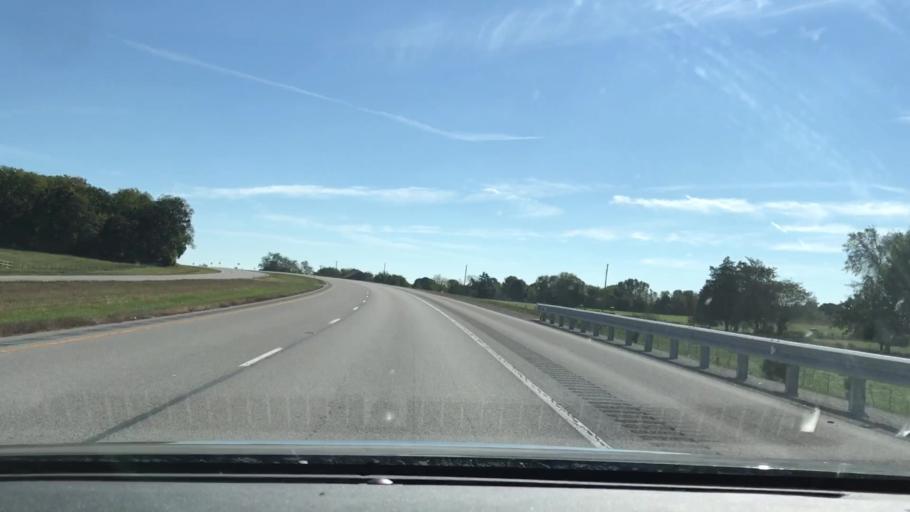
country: US
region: Kentucky
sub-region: Todd County
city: Elkton
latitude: 36.8100
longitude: -87.1353
